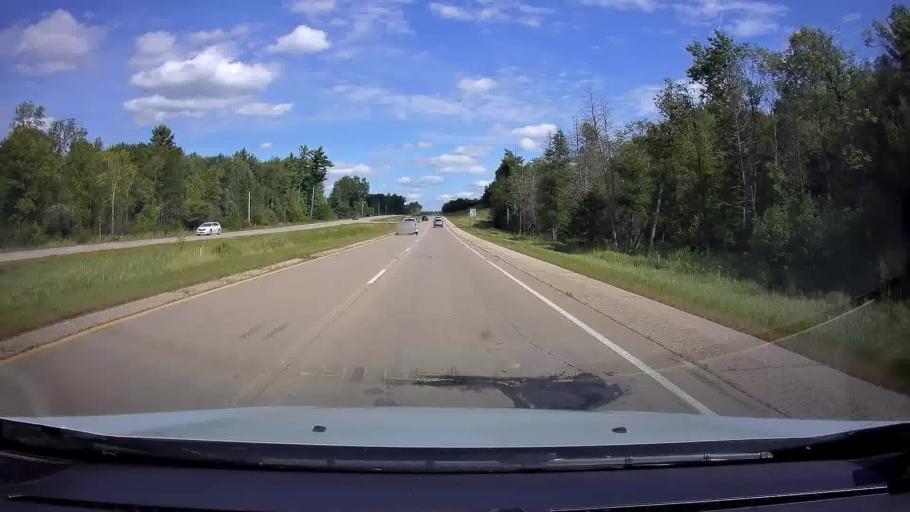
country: US
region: Wisconsin
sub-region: Waupaca County
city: Marion
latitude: 44.7966
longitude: -88.8073
